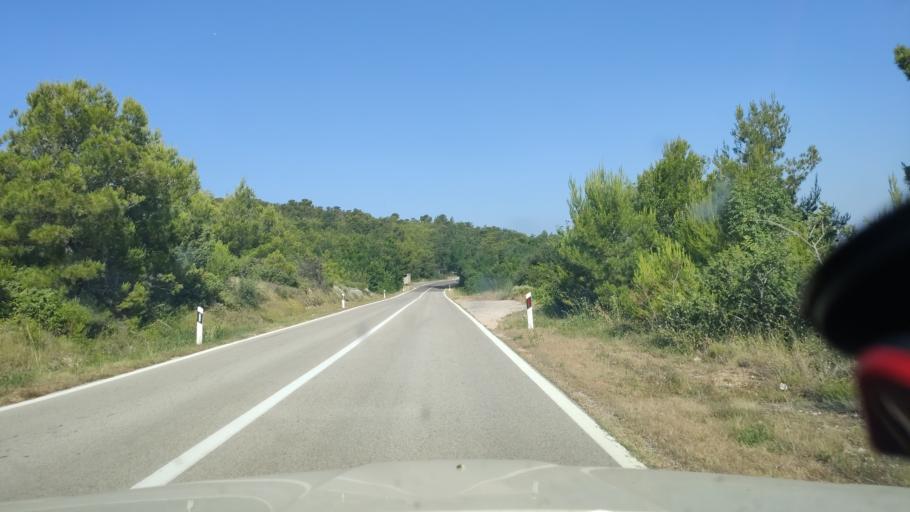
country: HR
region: Sibensko-Kniniska
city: Zaton
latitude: 43.9159
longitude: 15.8287
